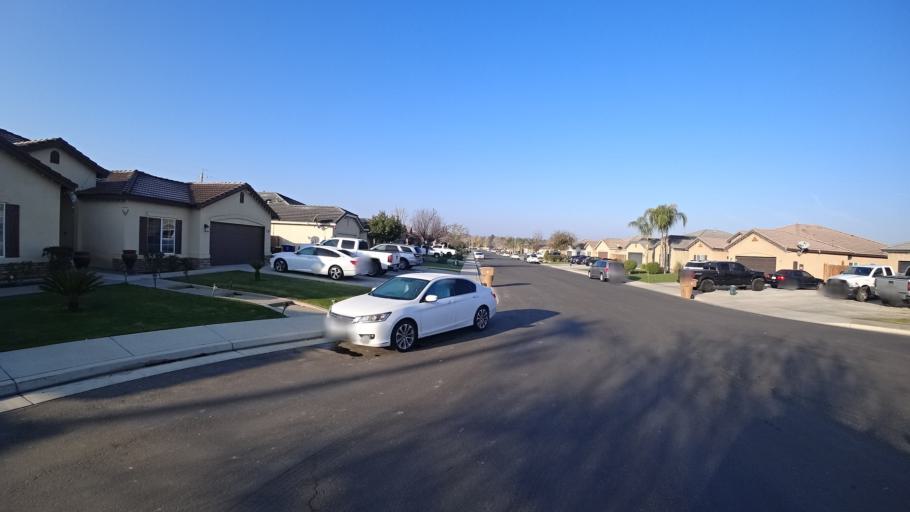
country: US
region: California
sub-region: Kern County
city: Greenacres
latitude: 35.2895
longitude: -119.1191
